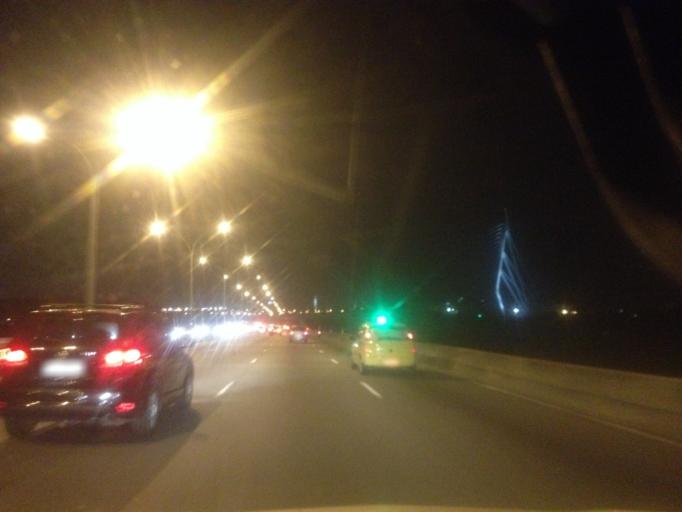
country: BR
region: Rio de Janeiro
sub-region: Rio De Janeiro
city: Rio de Janeiro
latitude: -22.8709
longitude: -43.2323
